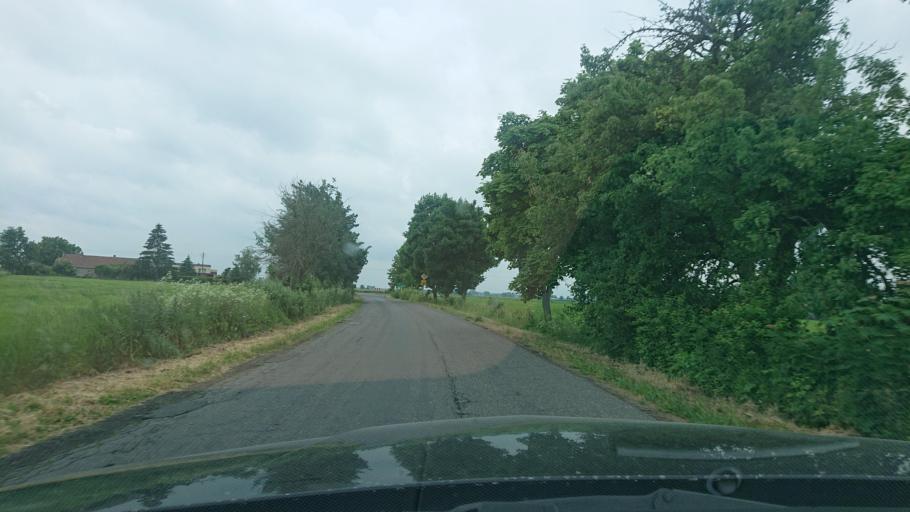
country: PL
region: Greater Poland Voivodeship
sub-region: Powiat gnieznienski
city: Czerniejewo
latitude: 52.4504
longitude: 17.5515
